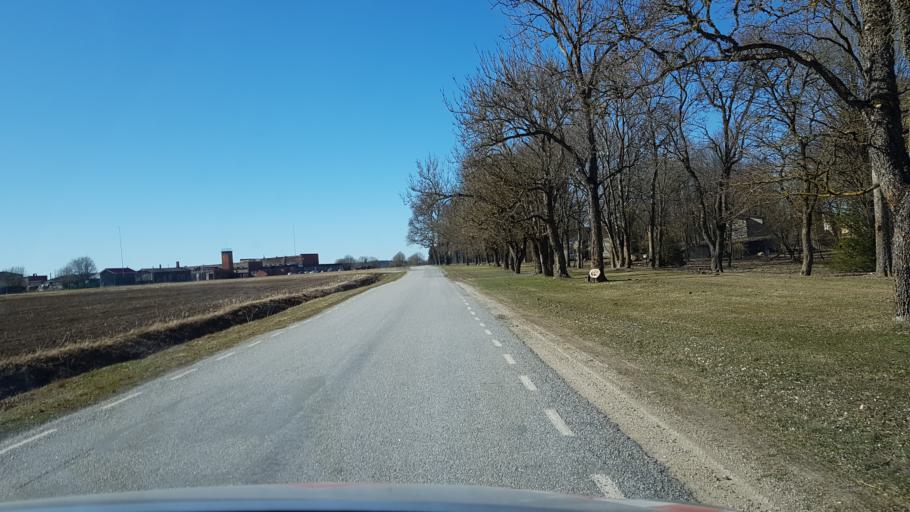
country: EE
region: Laeaene-Virumaa
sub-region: Viru-Nigula vald
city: Kunda
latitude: 59.3919
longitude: 26.5685
